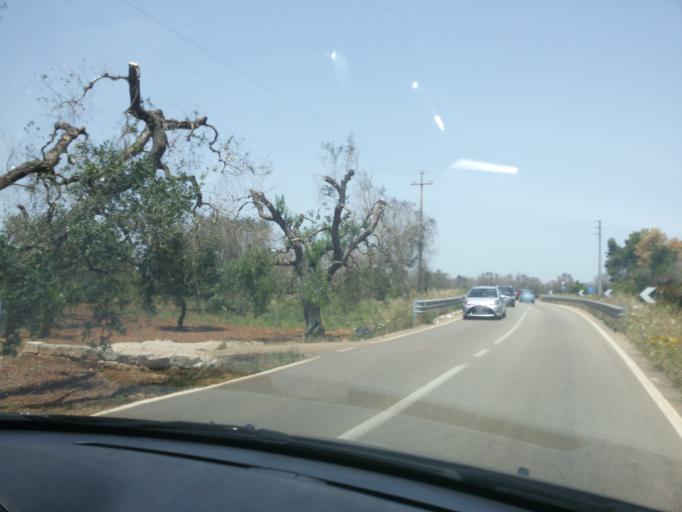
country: IT
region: Apulia
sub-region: Provincia di Lecce
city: Veglie
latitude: 40.3254
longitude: 17.9253
